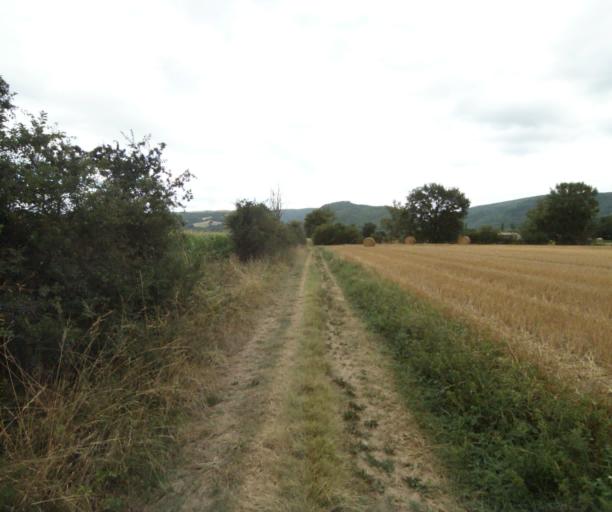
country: FR
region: Midi-Pyrenees
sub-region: Departement du Tarn
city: Soreze
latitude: 43.4599
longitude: 2.0487
